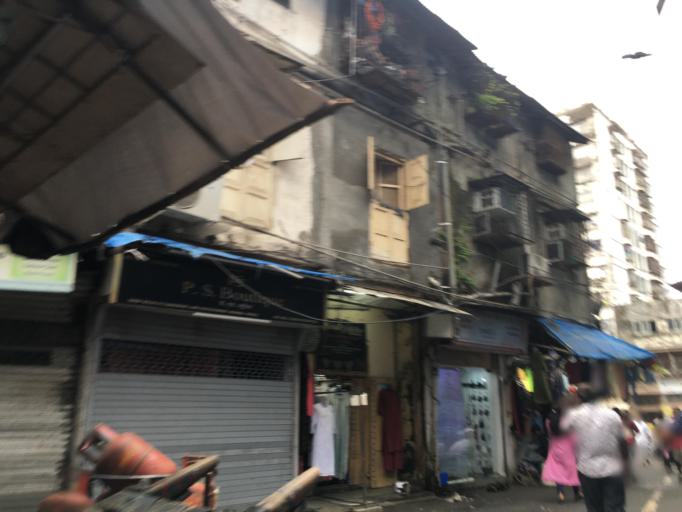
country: IN
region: Maharashtra
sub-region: Mumbai Suburban
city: Mumbai
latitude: 18.9520
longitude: 72.8270
